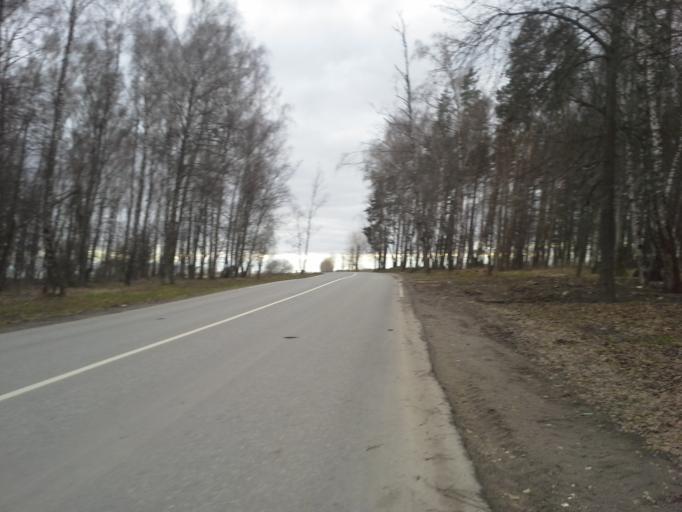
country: RU
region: Moskovskaya
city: Kommunarka
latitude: 55.5208
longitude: 37.4682
